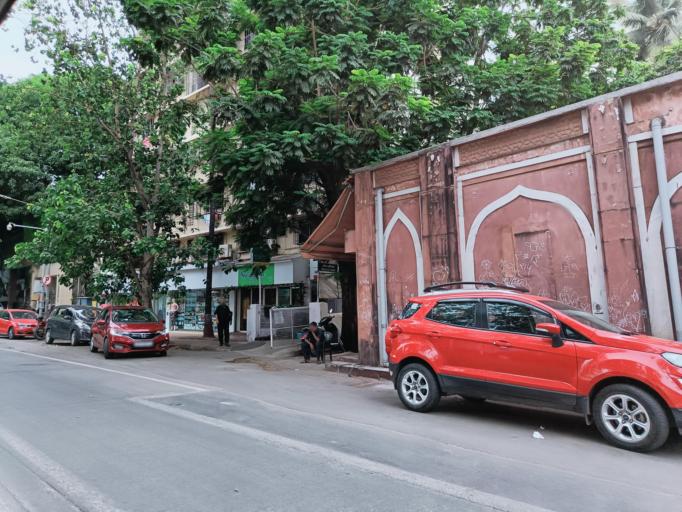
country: IN
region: Maharashtra
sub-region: Mumbai Suburban
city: Mumbai
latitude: 19.1079
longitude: 72.8264
